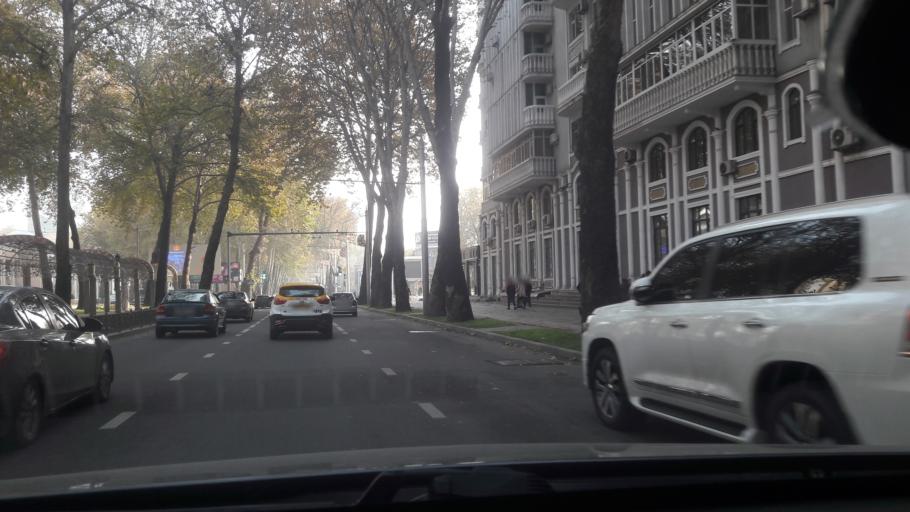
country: TJ
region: Dushanbe
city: Dushanbe
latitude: 38.5722
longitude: 68.7883
